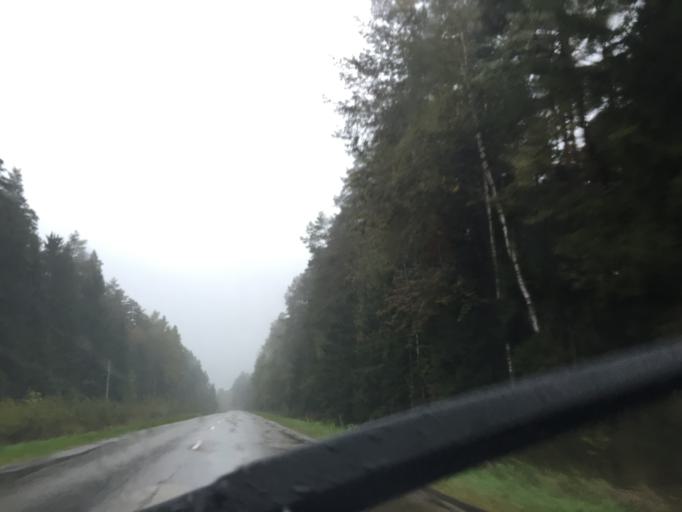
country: LV
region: Ropazu
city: Ropazi
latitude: 56.9856
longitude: 24.6348
